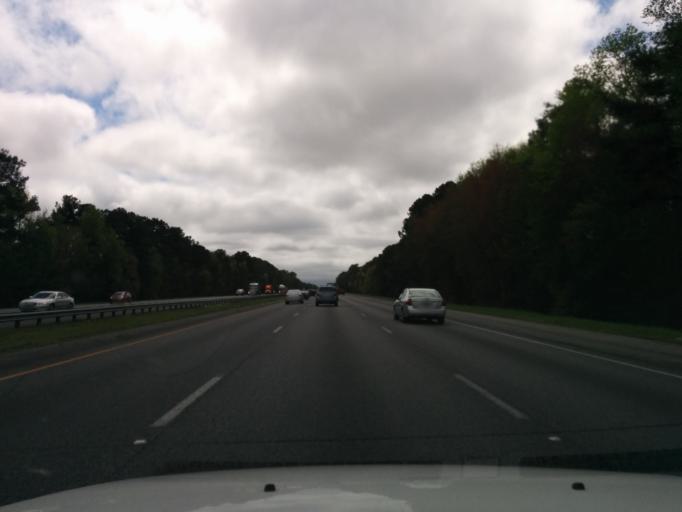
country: US
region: Georgia
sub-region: Chatham County
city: Pooler
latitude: 32.0520
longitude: -81.2573
